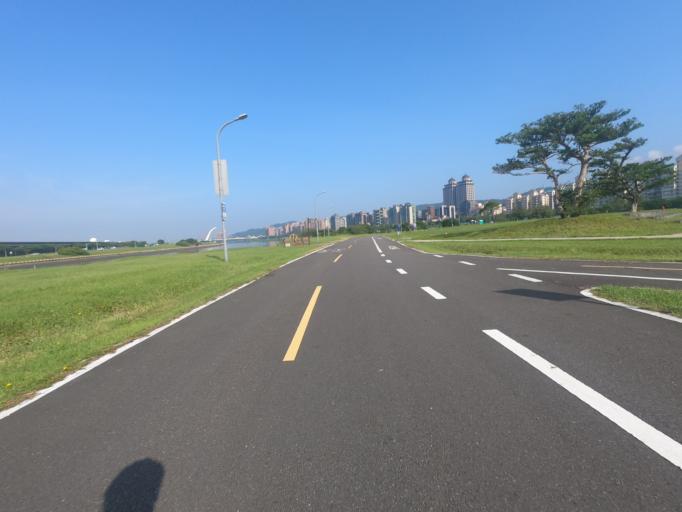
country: TW
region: Taipei
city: Taipei
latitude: 25.0739
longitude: 121.5607
